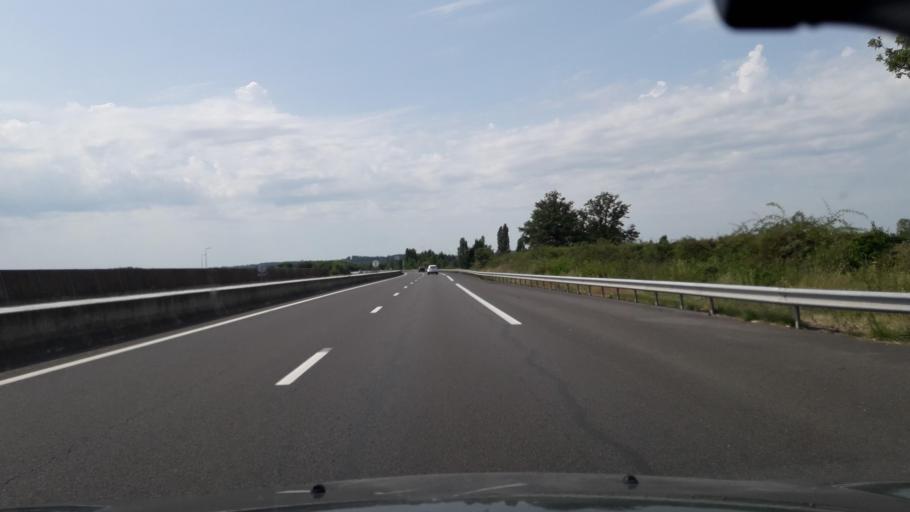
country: FR
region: Auvergne
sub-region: Departement de l'Allier
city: Domerat
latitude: 46.3631
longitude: 2.5545
